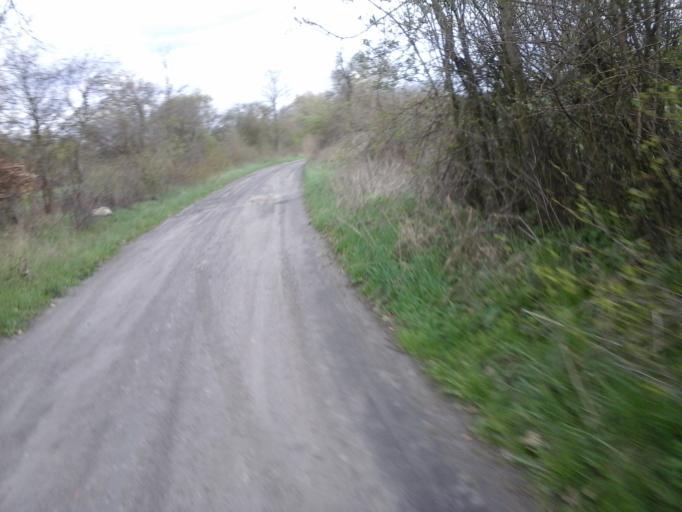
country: PL
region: West Pomeranian Voivodeship
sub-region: Powiat choszczenski
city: Krzecin
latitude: 53.0751
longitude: 15.5666
